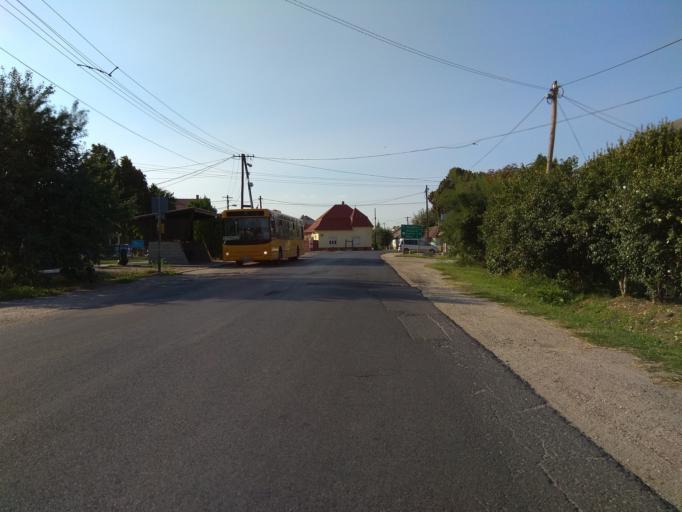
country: HU
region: Borsod-Abauj-Zemplen
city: Onod
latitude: 48.0017
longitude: 20.9175
